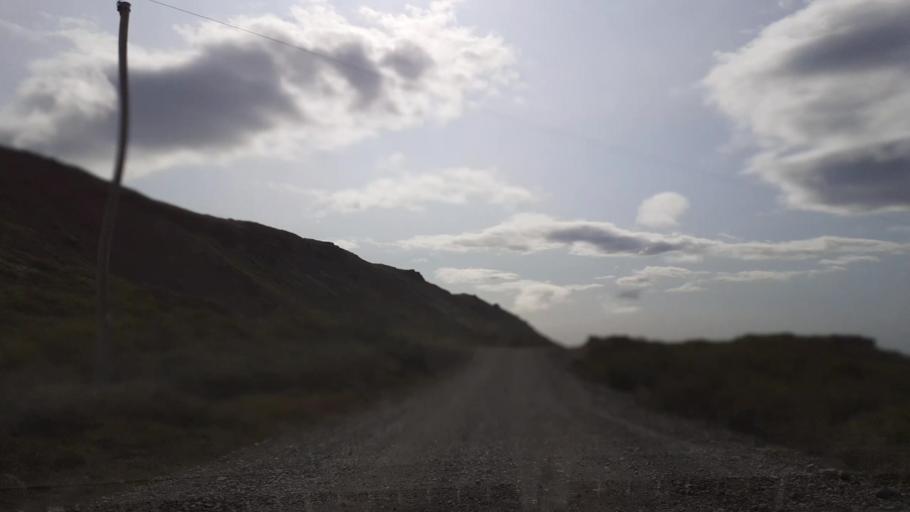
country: IS
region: East
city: Hoefn
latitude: 64.4303
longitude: -14.8876
